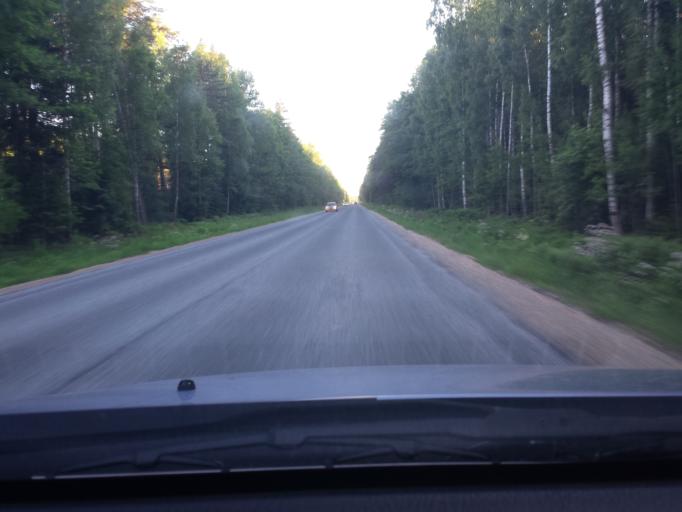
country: LV
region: Carnikava
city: Carnikava
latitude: 57.1077
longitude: 24.2225
